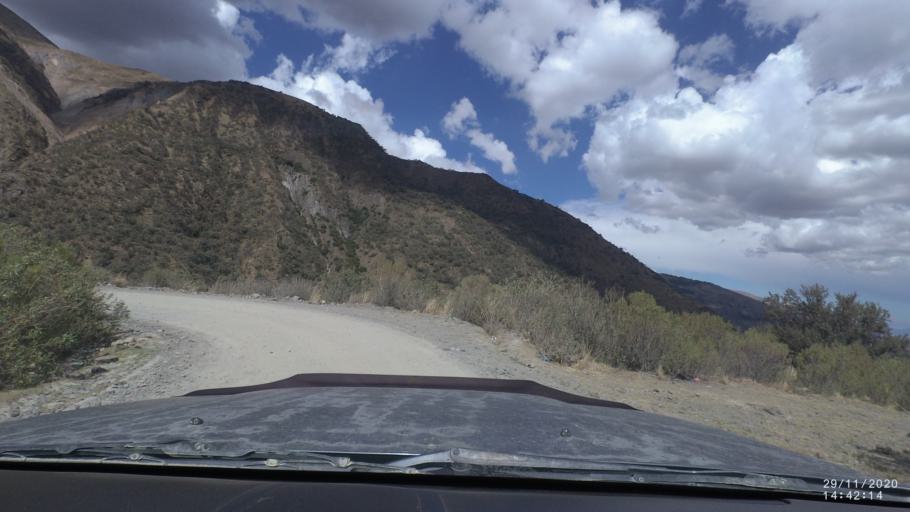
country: BO
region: Cochabamba
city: Sipe Sipe
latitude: -17.2779
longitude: -66.3213
